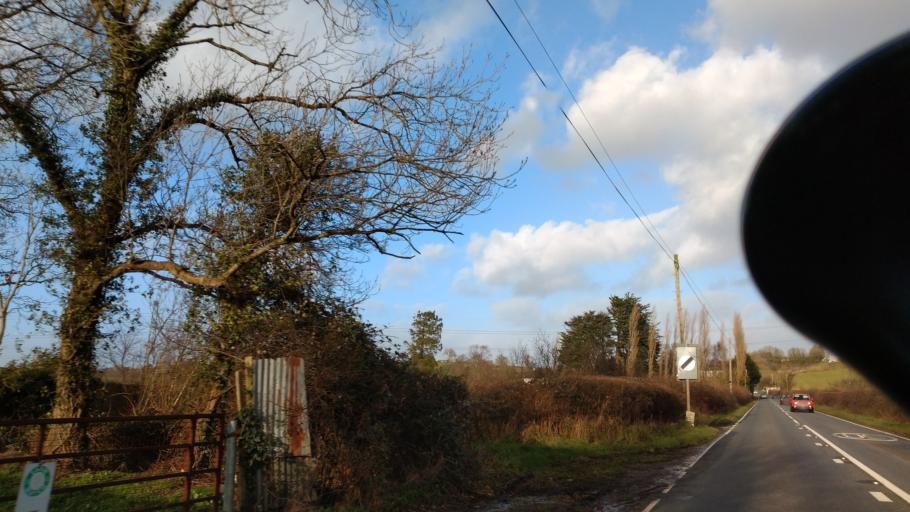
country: GB
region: England
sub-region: Somerset
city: Shepton Mallet
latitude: 51.1580
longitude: -2.5420
